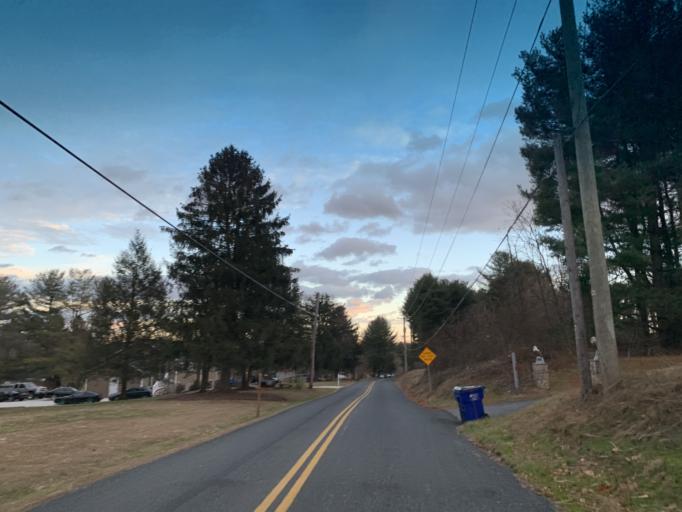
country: US
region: Pennsylvania
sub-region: York County
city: Susquehanna Trails
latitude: 39.6596
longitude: -76.3101
